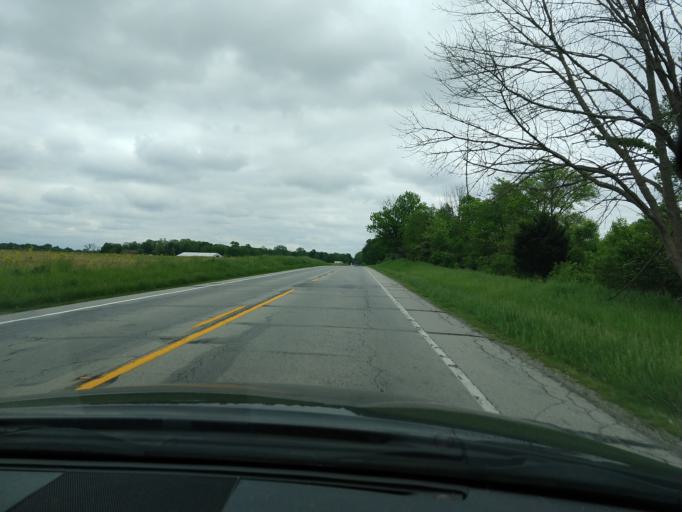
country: US
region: Indiana
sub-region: Hamilton County
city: Noblesville
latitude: 40.0471
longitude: -85.9540
